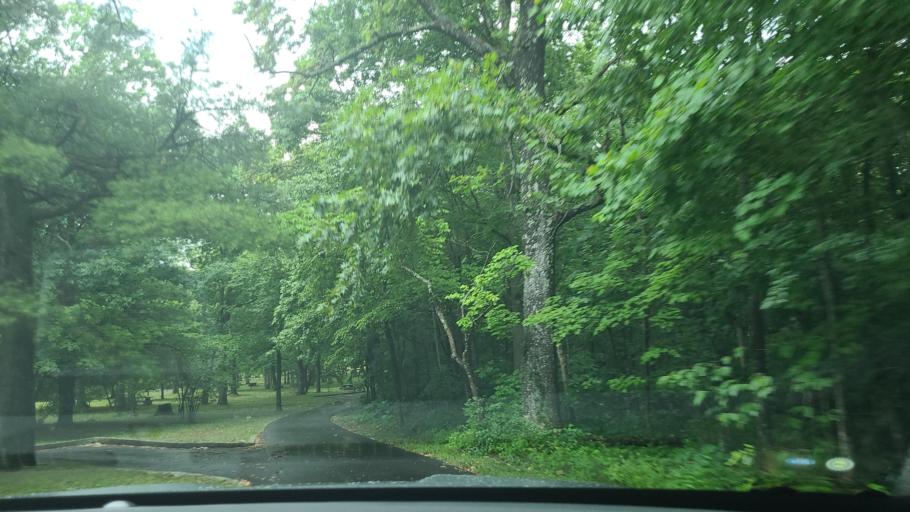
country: US
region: Virginia
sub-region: Floyd County
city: Floyd
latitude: 36.9297
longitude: -80.1848
